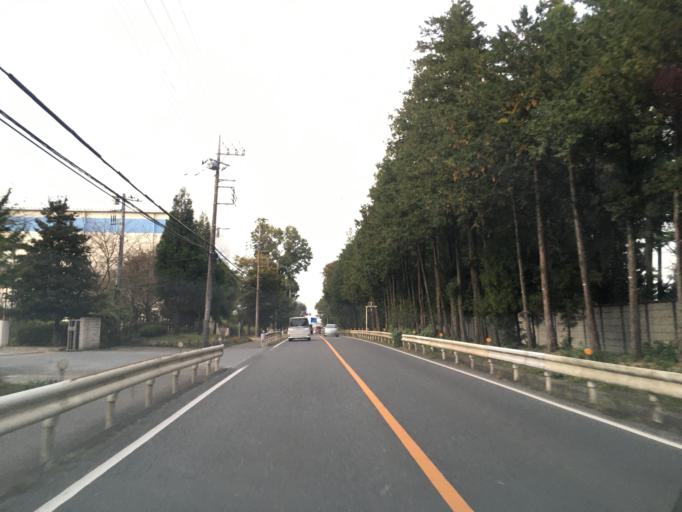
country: JP
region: Saitama
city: Sayama
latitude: 35.8913
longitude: 139.3782
